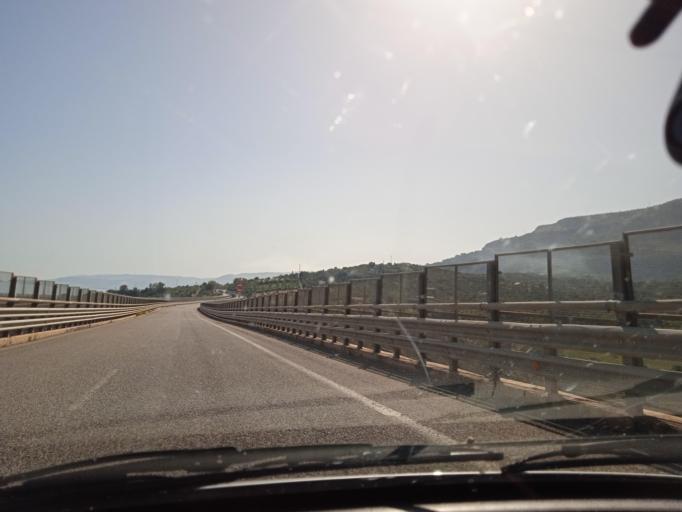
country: IT
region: Sicily
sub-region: Messina
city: Acquedolci
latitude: 38.0458
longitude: 14.5556
